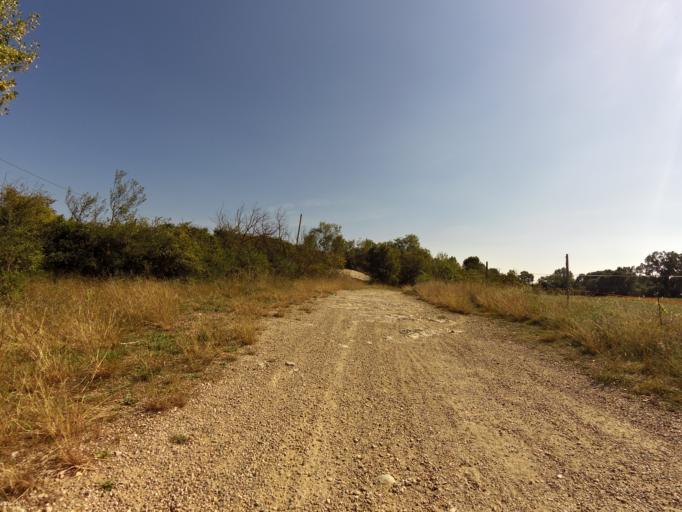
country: FR
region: Languedoc-Roussillon
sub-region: Departement de l'Herault
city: Villetelle
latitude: 43.7260
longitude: 4.1505
